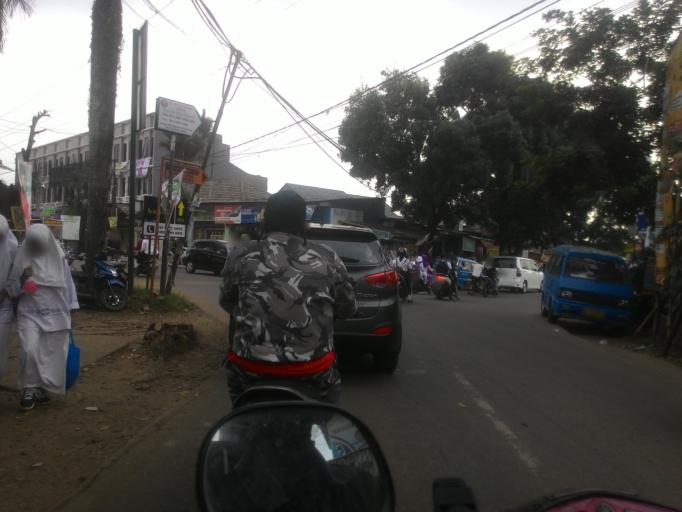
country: ID
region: West Java
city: Cibinong
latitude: -6.4461
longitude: 106.8289
